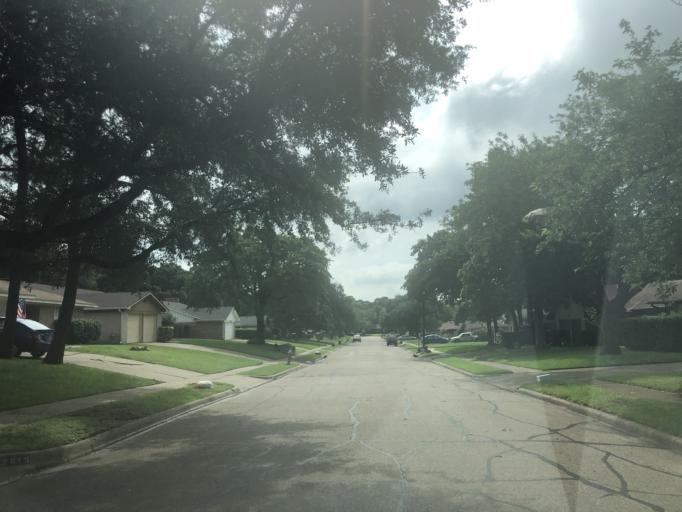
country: US
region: Texas
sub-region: Dallas County
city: Irving
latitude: 32.7991
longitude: -96.9716
